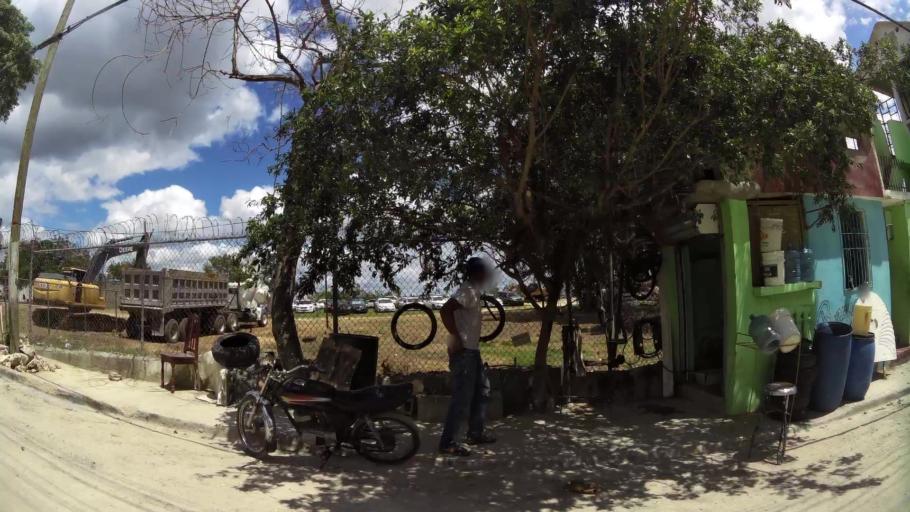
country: DO
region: Nacional
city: Ensanche Luperon
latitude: 18.5169
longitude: -69.9038
